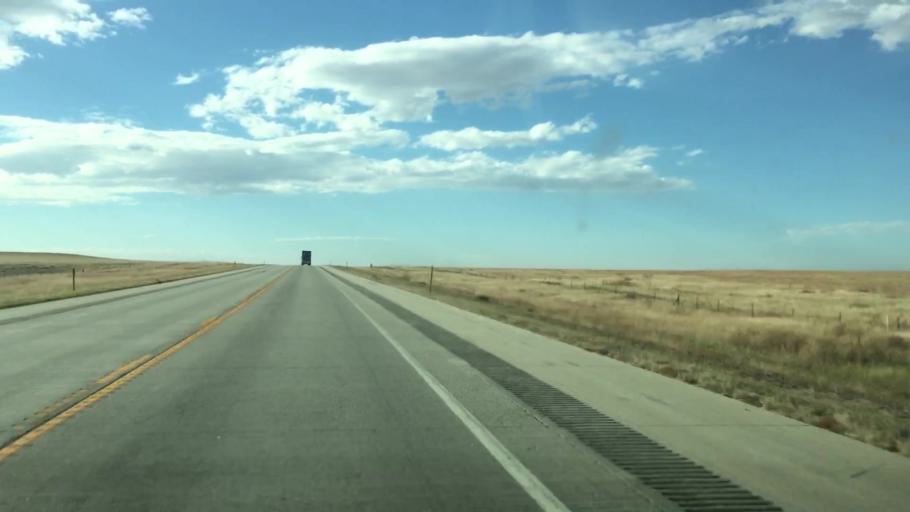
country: US
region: Colorado
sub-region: Lincoln County
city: Hugo
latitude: 39.1913
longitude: -103.5625
